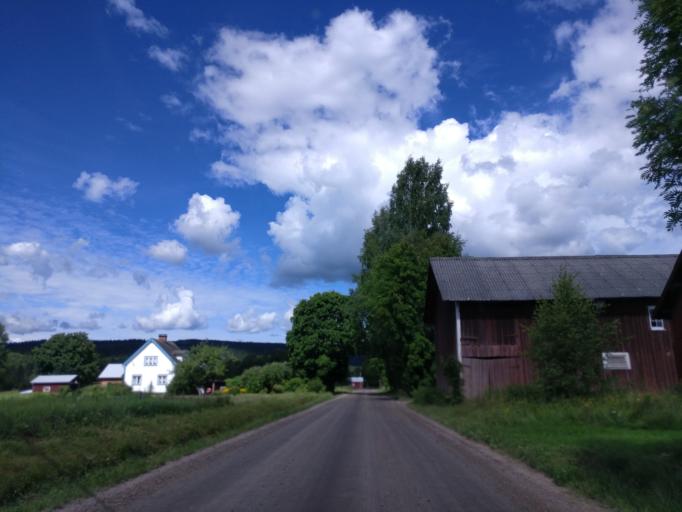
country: SE
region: Vaermland
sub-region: Hagfors Kommun
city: Ekshaerad
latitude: 60.0488
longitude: 13.4884
